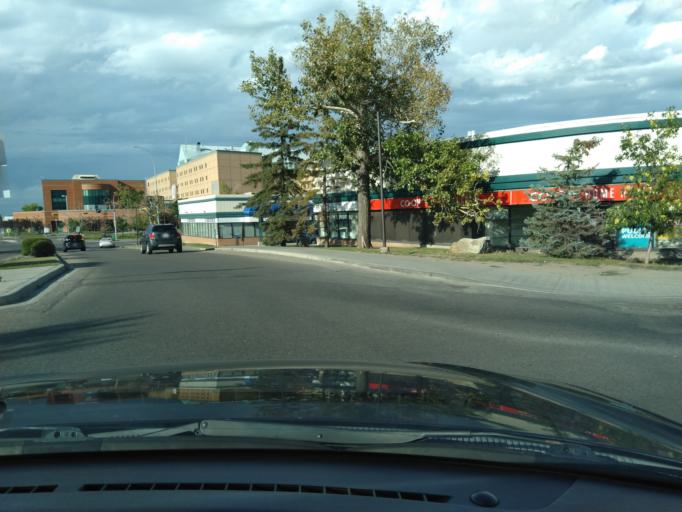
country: CA
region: Alberta
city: Calgary
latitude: 51.0769
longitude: -113.9853
